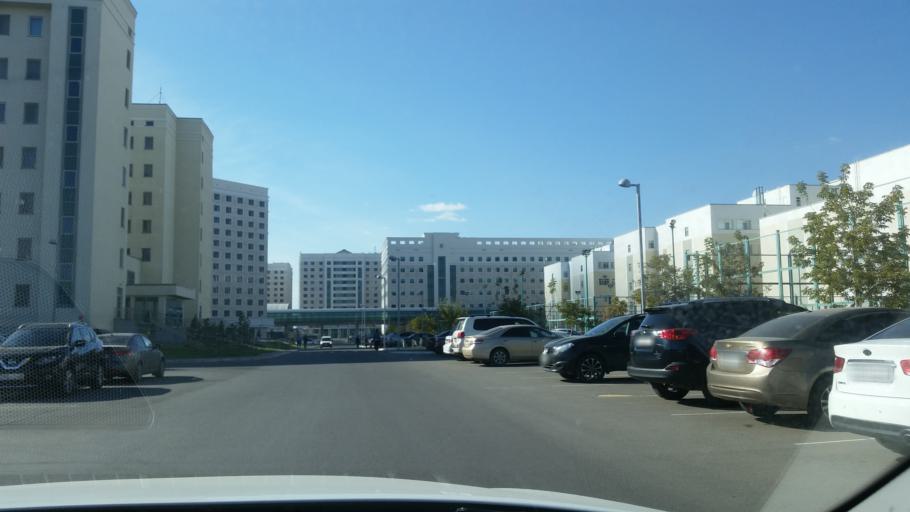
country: KZ
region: Astana Qalasy
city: Astana
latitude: 51.0890
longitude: 71.3999
